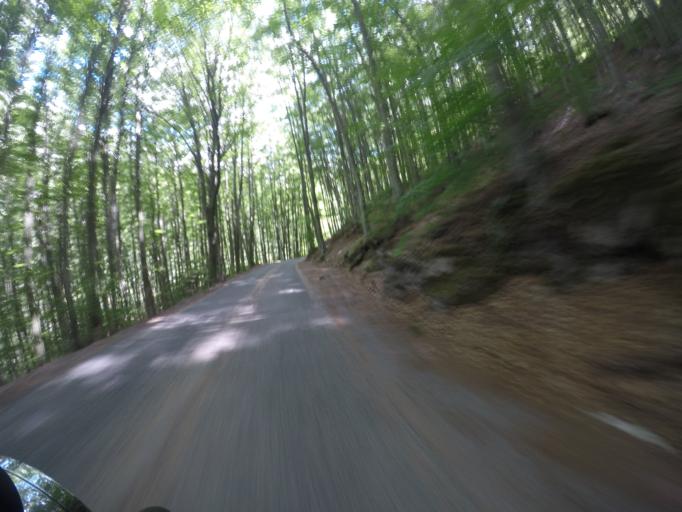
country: IT
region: Tuscany
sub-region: Provincia di Lucca
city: Minucciano
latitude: 44.1472
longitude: 10.1951
